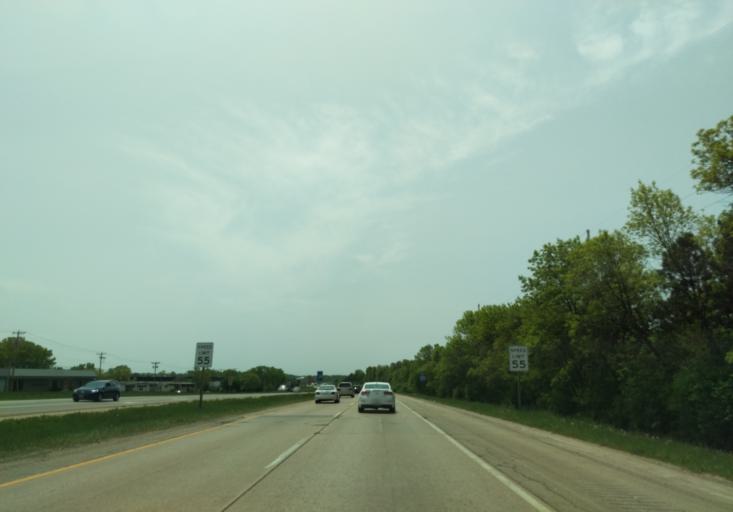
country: US
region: Wisconsin
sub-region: Dane County
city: Monona
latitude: 43.0612
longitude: -89.3096
